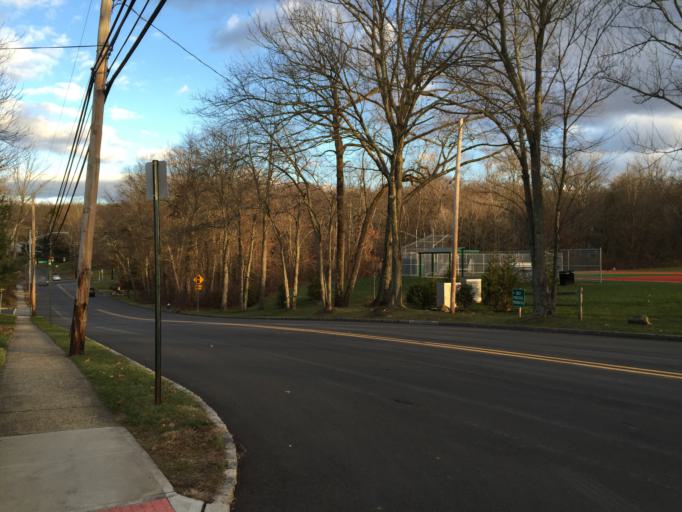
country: US
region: New Jersey
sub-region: Union County
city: New Providence
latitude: 40.6999
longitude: -74.3915
